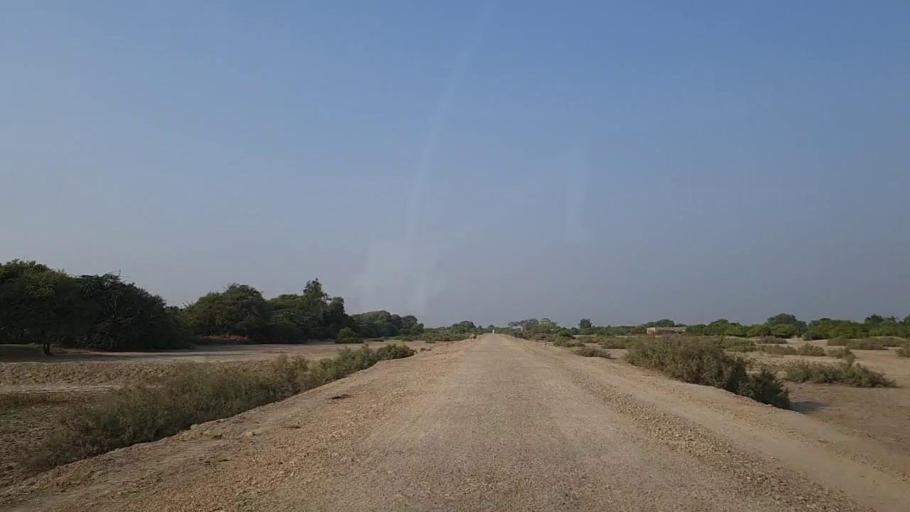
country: PK
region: Sindh
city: Mirpur Sakro
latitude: 24.6429
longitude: 67.7676
